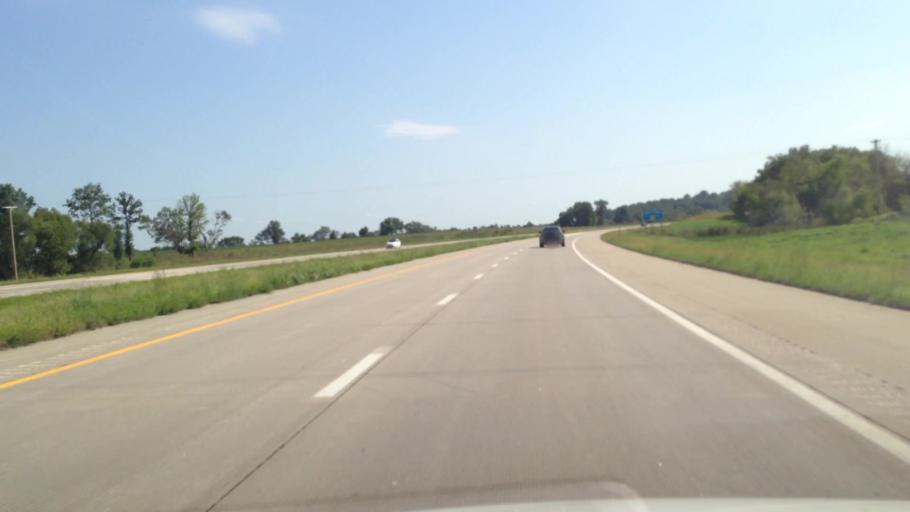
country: US
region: Kansas
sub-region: Linn County
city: Pleasanton
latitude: 38.2734
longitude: -94.6684
